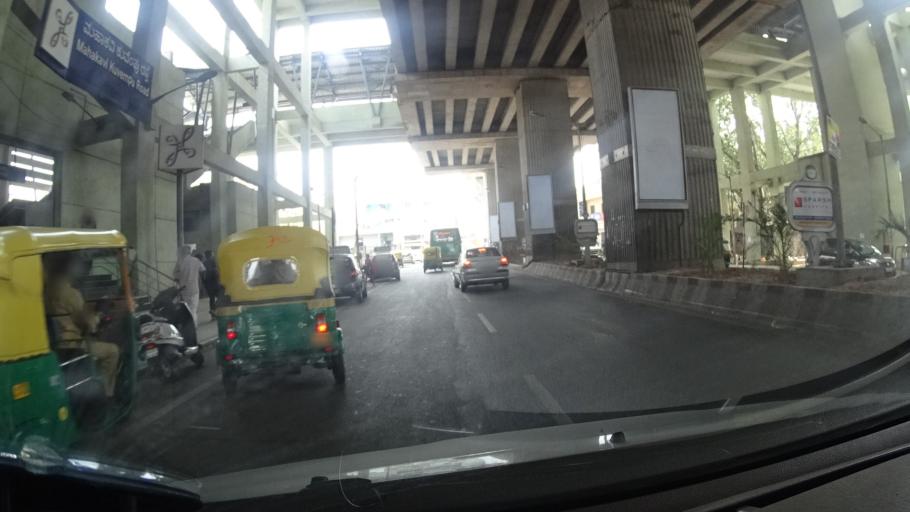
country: IN
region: Karnataka
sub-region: Bangalore Urban
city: Bangalore
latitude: 12.9985
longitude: 77.5570
